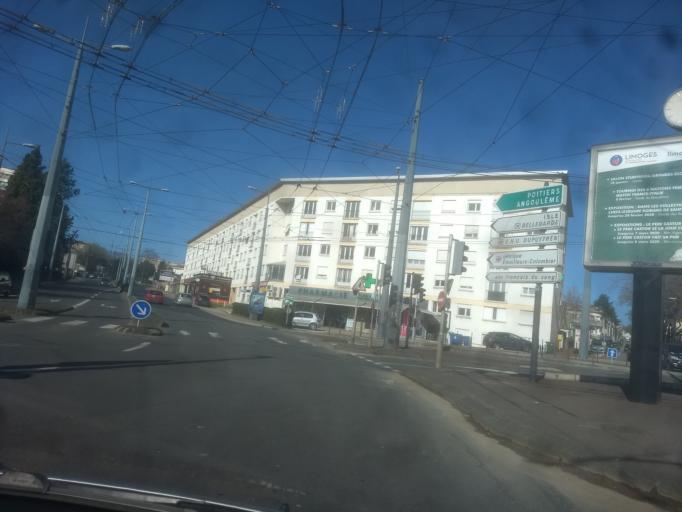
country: FR
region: Limousin
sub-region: Departement de la Haute-Vienne
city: Limoges
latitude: 45.8187
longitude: 1.2521
